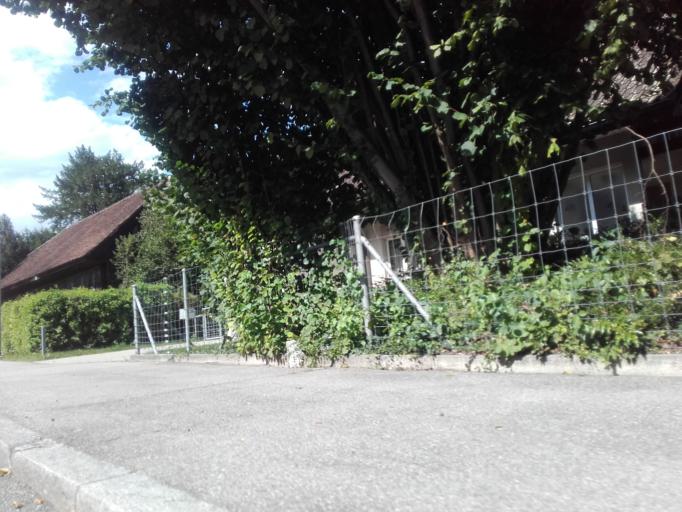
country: CH
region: Solothurn
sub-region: Bezirk Solothurn
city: Solothurn
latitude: 47.2136
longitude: 7.5483
